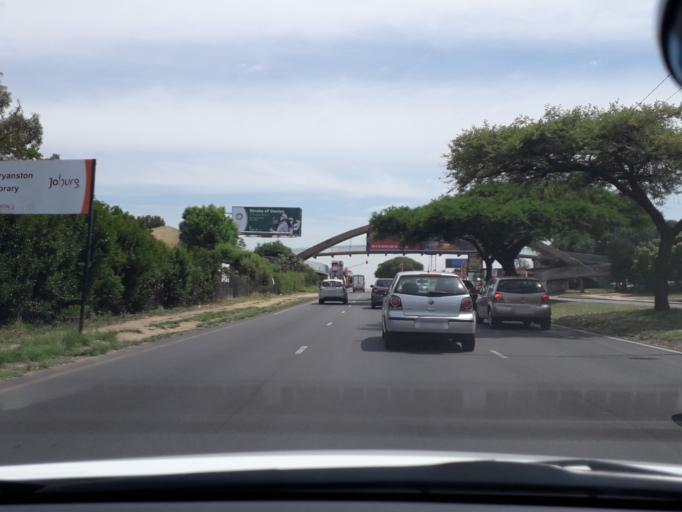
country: ZA
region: Gauteng
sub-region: City of Johannesburg Metropolitan Municipality
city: Midrand
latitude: -26.0619
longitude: 28.0238
